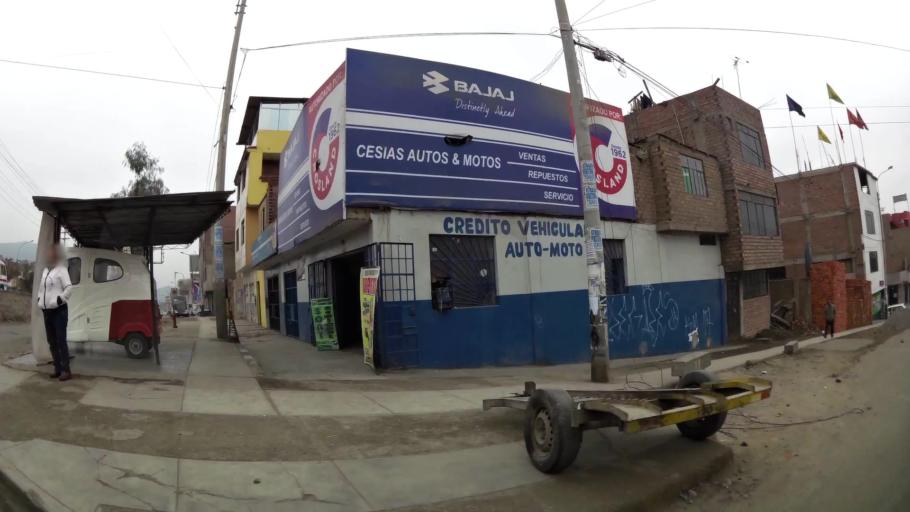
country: PE
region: Lima
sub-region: Lima
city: Urb. Santo Domingo
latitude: -11.8934
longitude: -77.0289
